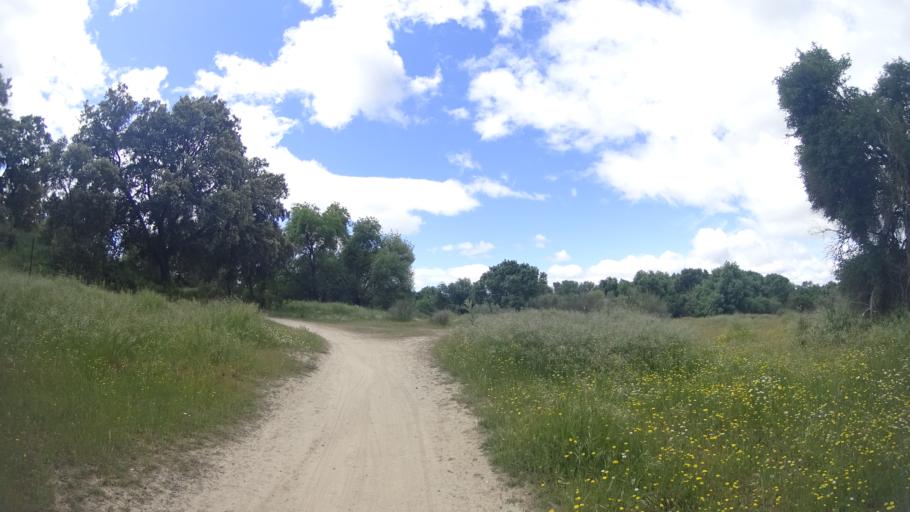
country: ES
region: Madrid
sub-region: Provincia de Madrid
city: Brunete
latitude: 40.3922
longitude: -3.9452
